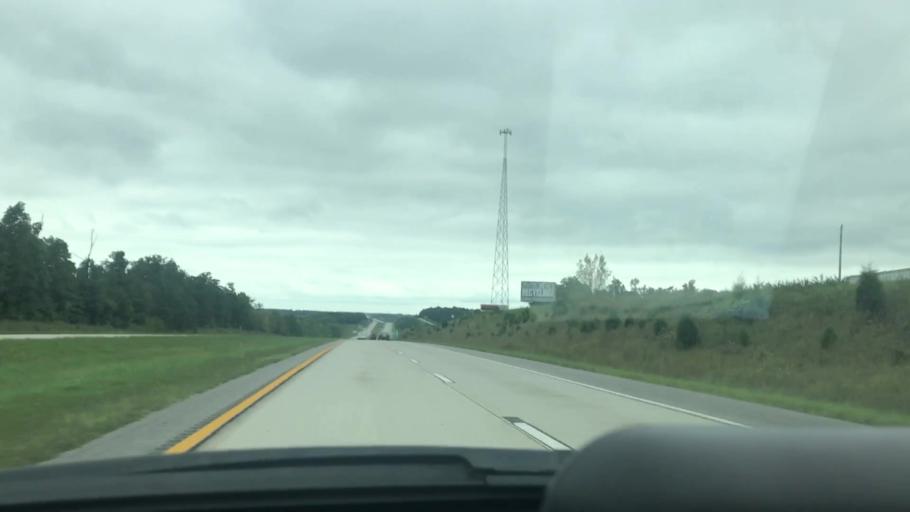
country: US
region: Missouri
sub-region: Greene County
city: Fair Grove
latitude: 37.5070
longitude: -93.1388
